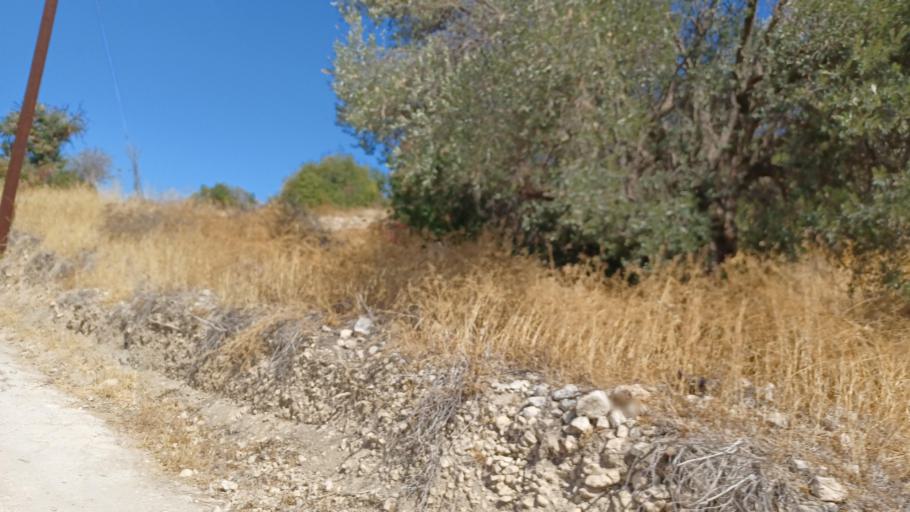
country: CY
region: Pafos
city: Polis
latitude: 34.9714
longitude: 32.4994
